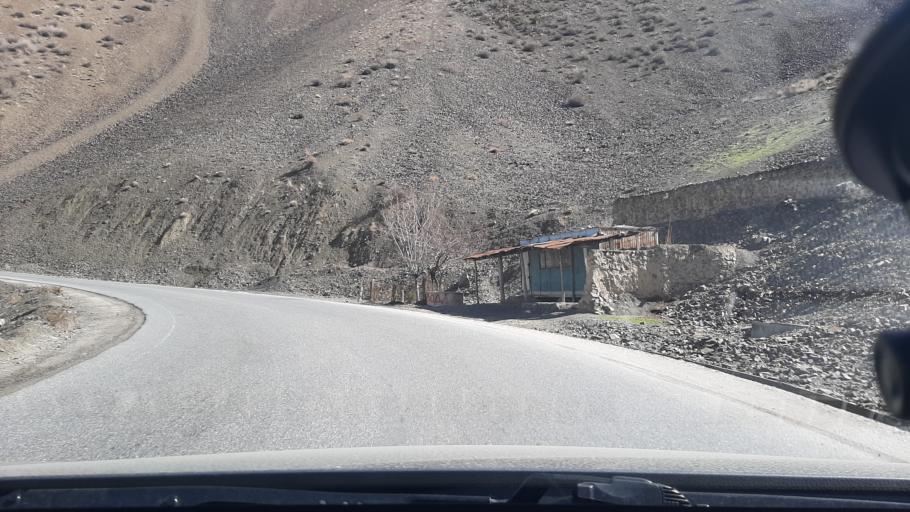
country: TJ
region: Viloyati Sughd
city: Ayni
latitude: 39.4595
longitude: 68.5587
